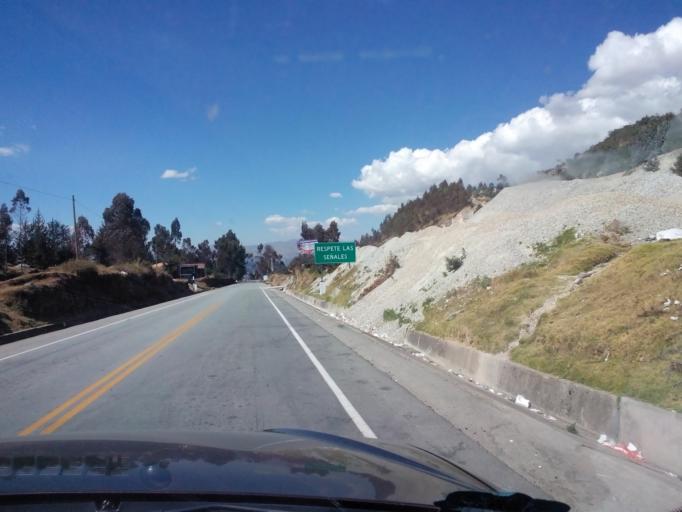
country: PE
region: Cusco
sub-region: Provincia de Anta
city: Ancahuasi
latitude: -13.4423
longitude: -72.3518
